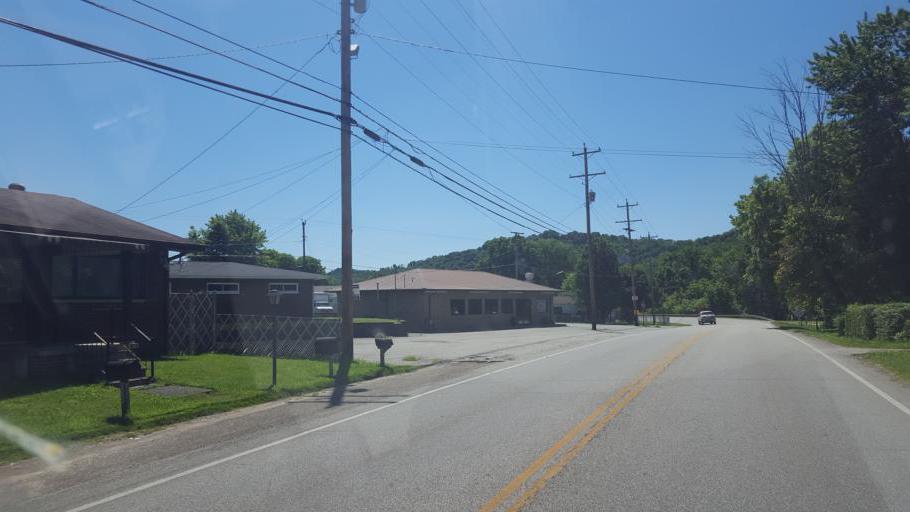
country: US
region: West Virginia
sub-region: Cabell County
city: Pea Ridge
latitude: 38.4421
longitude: -82.3544
